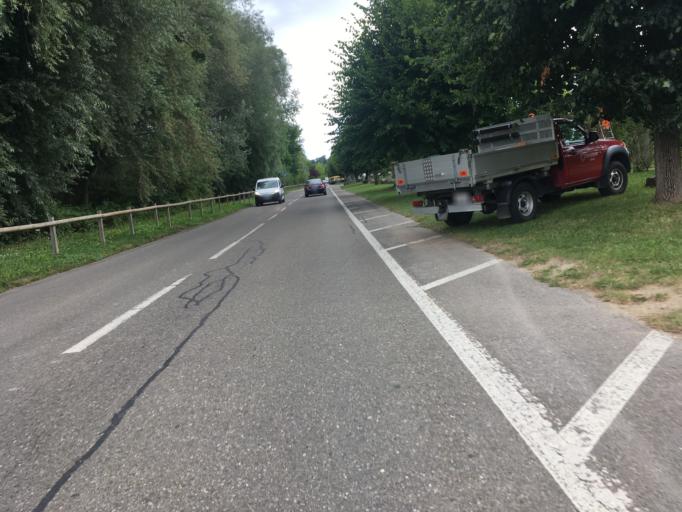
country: CH
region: Fribourg
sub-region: Broye District
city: Estavayer-le-Lac
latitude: 46.8535
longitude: 6.8467
